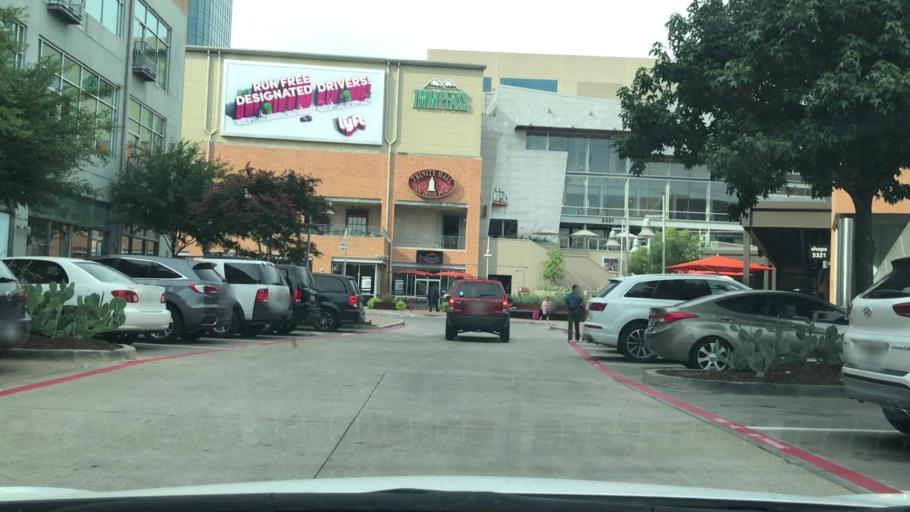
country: US
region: Texas
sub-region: Dallas County
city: Highland Park
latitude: 32.8375
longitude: -96.7760
